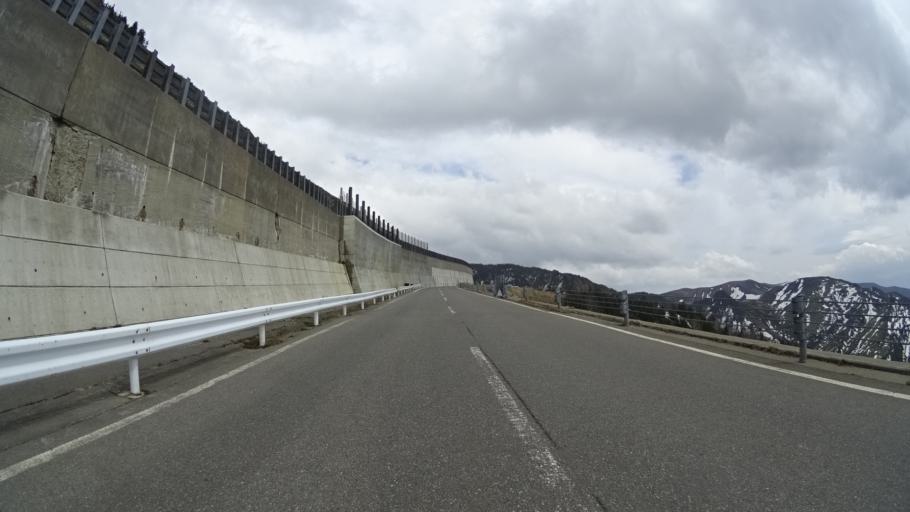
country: JP
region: Nagano
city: Nakano
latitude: 36.6693
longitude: 138.5209
